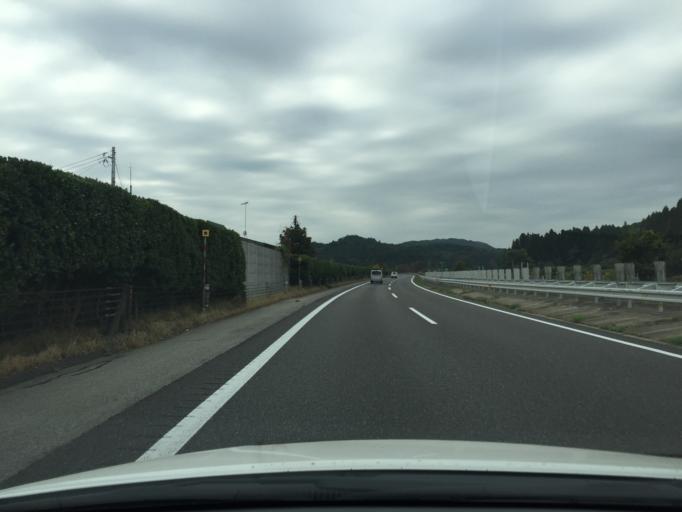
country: JP
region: Fukushima
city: Sukagawa
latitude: 37.1609
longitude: 140.2644
